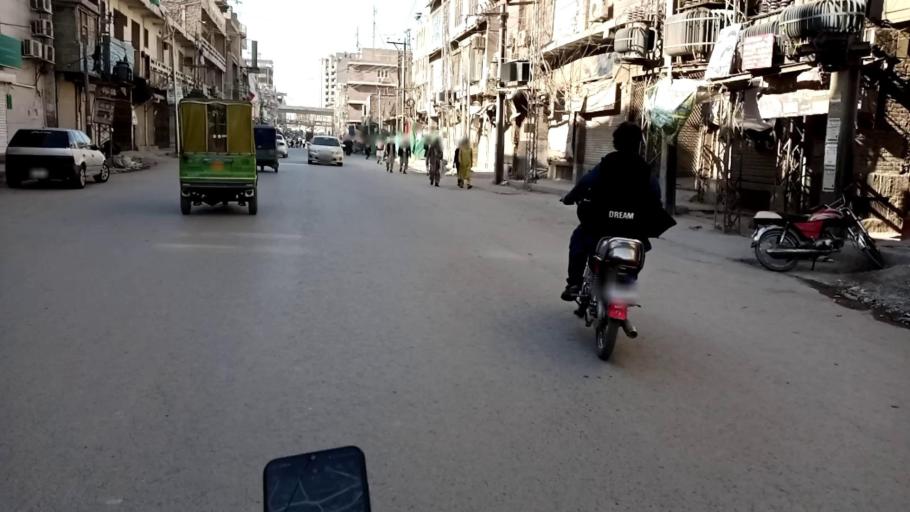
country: PK
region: Khyber Pakhtunkhwa
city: Peshawar
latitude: 34.0062
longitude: 71.5654
